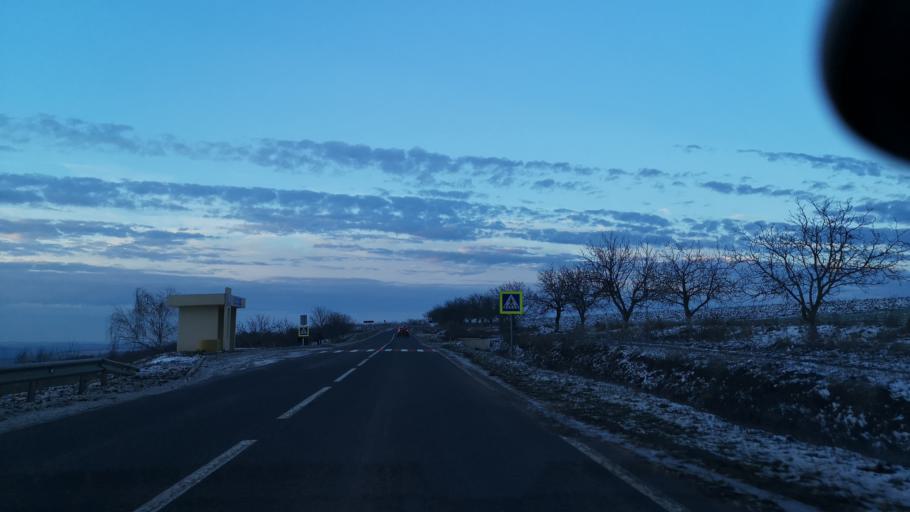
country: MD
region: Rezina
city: Saharna
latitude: 47.6043
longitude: 28.8313
